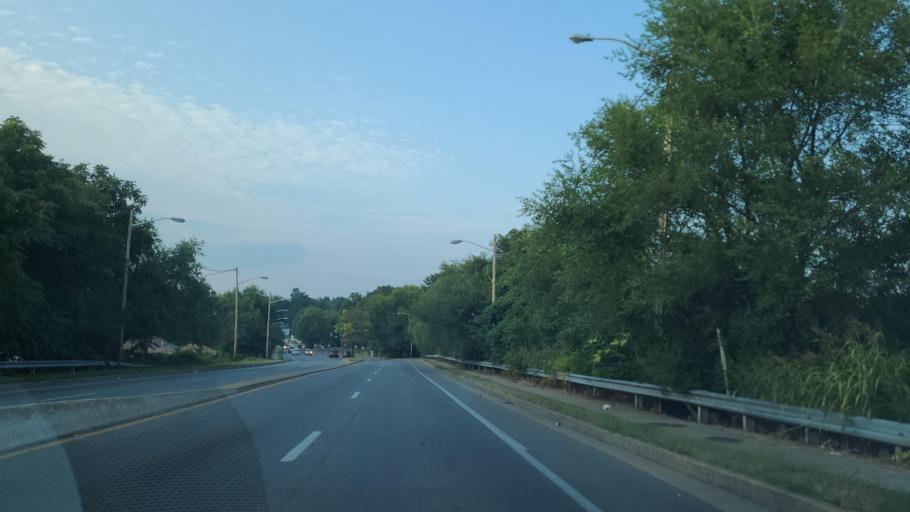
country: US
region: Virginia
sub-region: City of Roanoke
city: Roanoke
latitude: 37.2769
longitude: -79.9565
